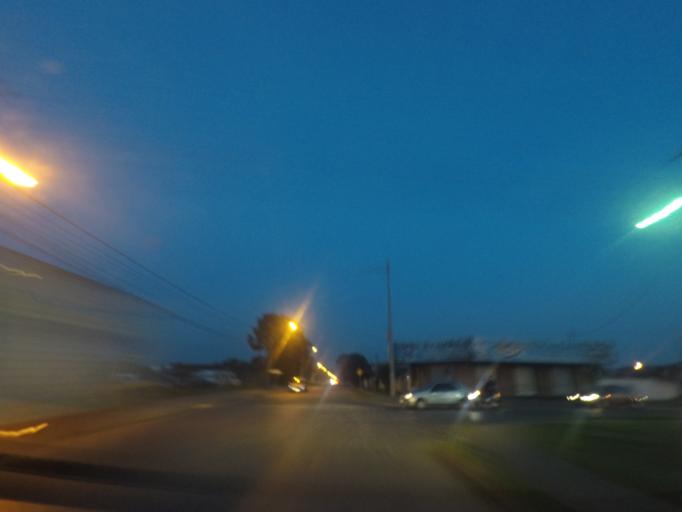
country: BR
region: Parana
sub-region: Pinhais
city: Pinhais
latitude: -25.4766
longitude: -49.1507
